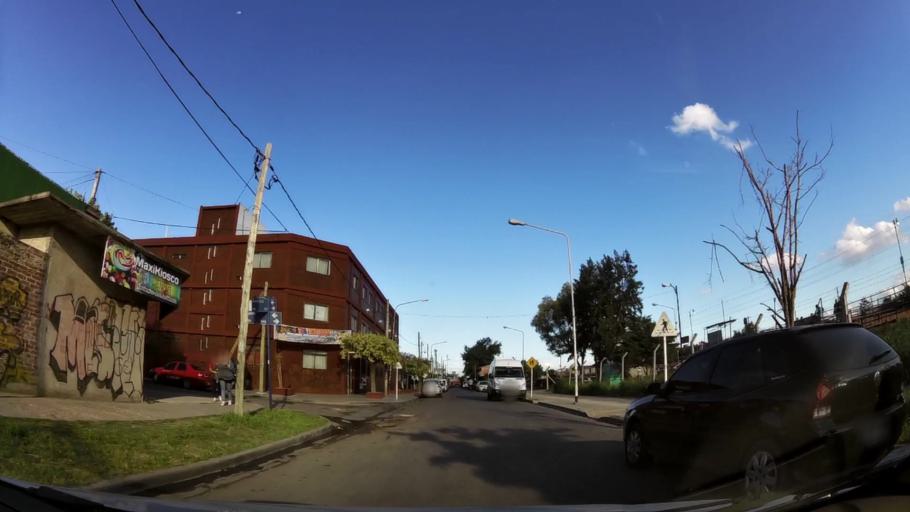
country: AR
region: Buenos Aires
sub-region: Partido de Moron
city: Moron
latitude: -34.6992
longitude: -58.6284
